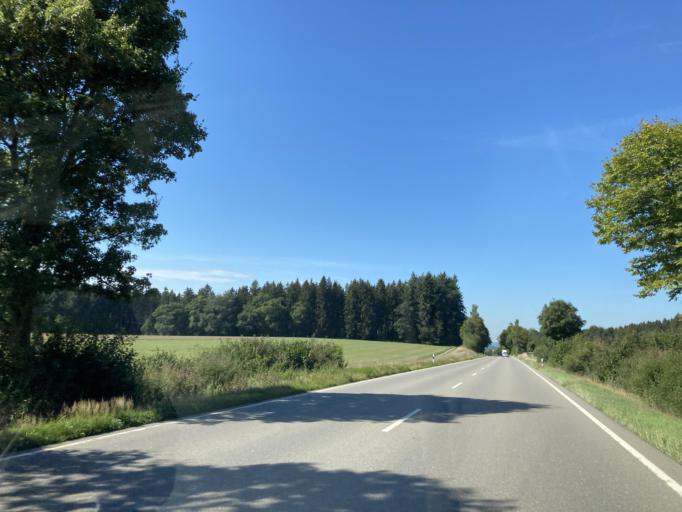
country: DE
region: Baden-Wuerttemberg
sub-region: Tuebingen Region
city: Betzenweiler
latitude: 48.1390
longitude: 9.5641
